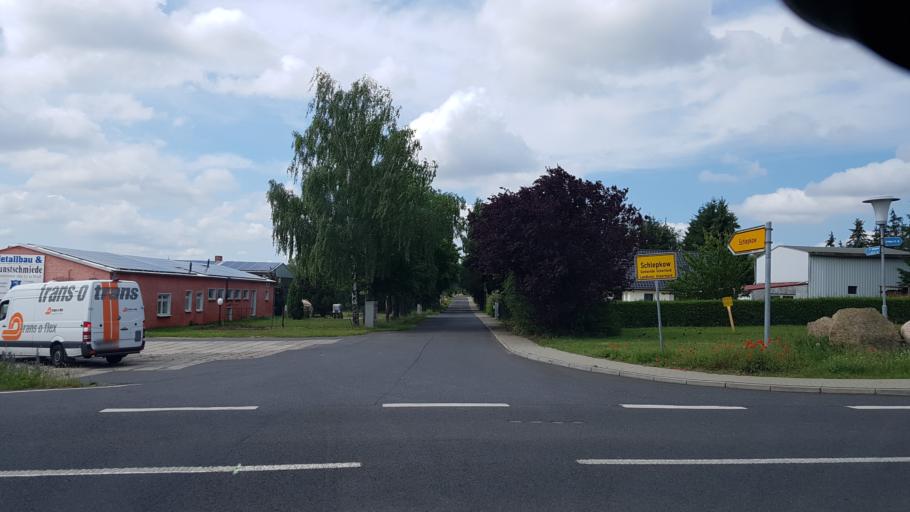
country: DE
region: Mecklenburg-Vorpommern
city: Strasburg
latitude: 53.4258
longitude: 13.6950
